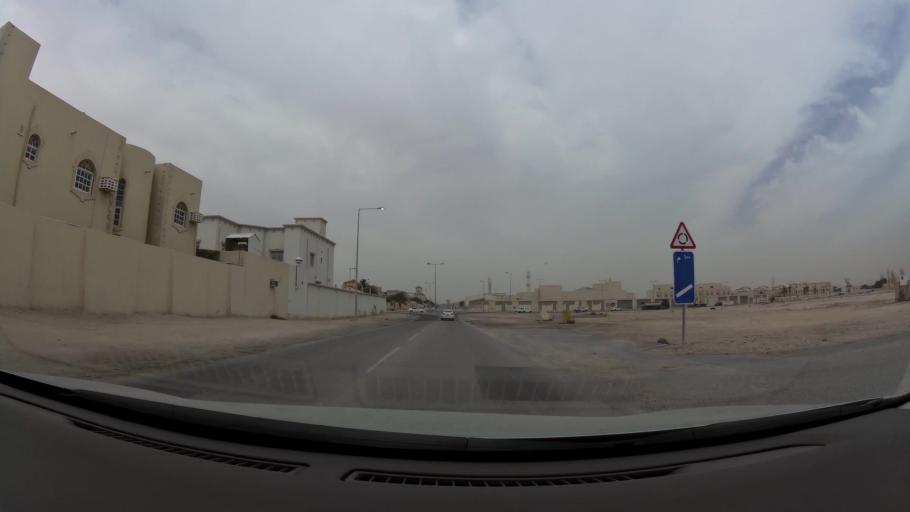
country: QA
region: Baladiyat ar Rayyan
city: Ar Rayyan
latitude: 25.2254
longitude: 51.4597
